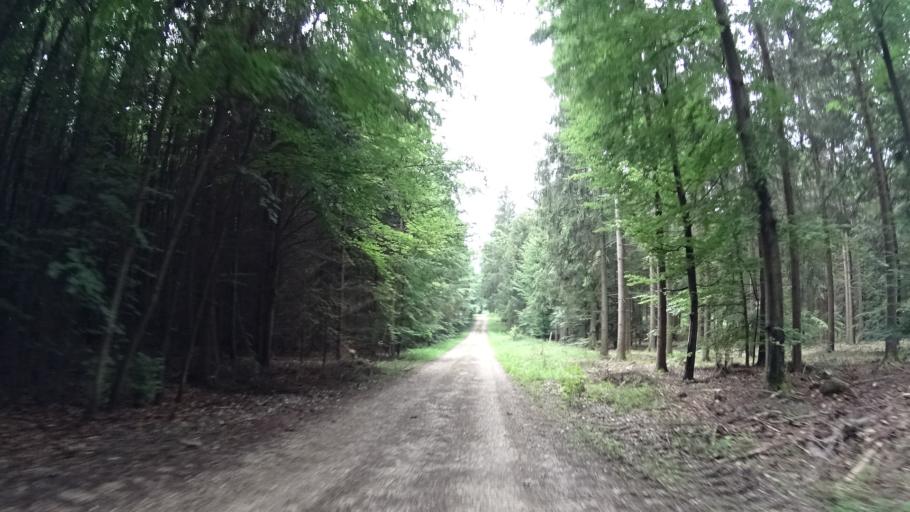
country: DE
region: Bavaria
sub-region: Upper Bavaria
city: Denkendorf
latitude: 48.8966
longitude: 11.4398
